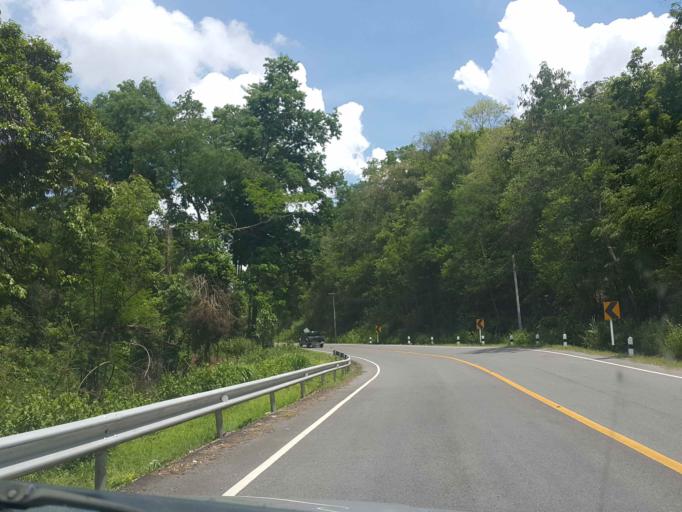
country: TH
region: Phayao
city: Chiang Muan
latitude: 18.8489
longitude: 100.3332
